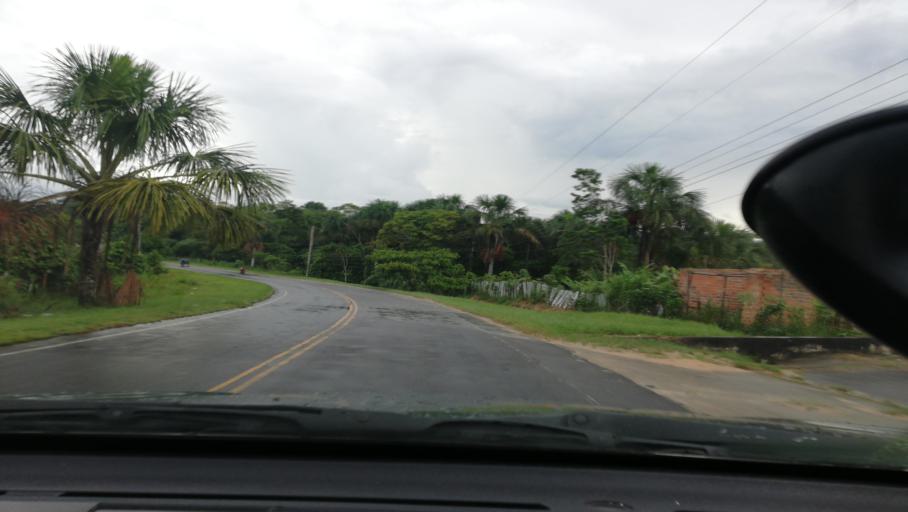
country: PE
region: Loreto
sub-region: Provincia de Maynas
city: Iquitos
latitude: -3.8657
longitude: -73.3417
